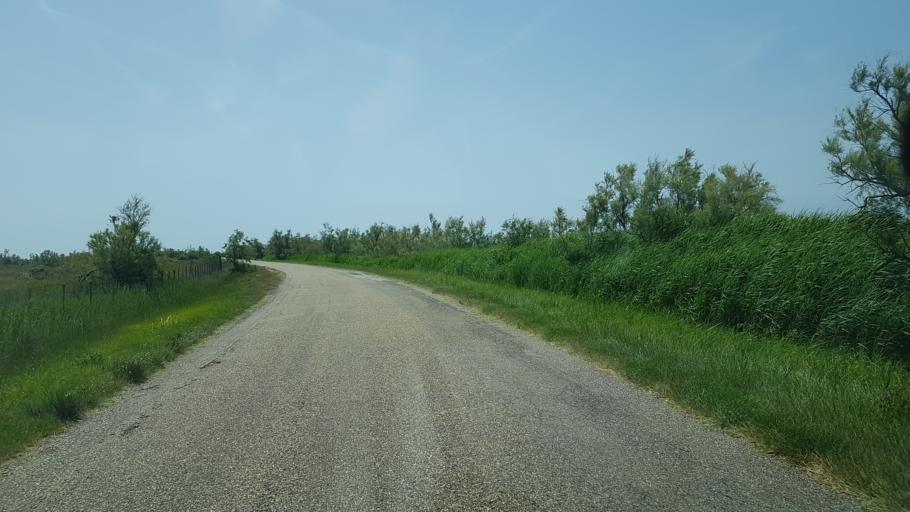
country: FR
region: Provence-Alpes-Cote d'Azur
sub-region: Departement des Bouches-du-Rhone
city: Arles
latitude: 43.4945
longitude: 4.6416
